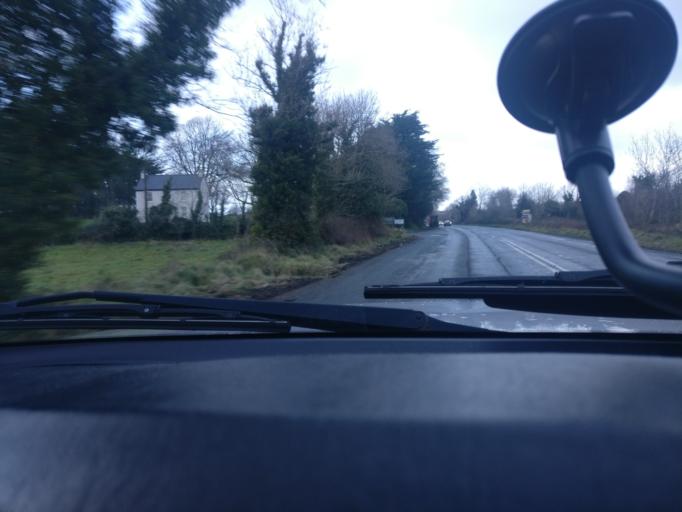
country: IE
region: Connaught
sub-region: County Galway
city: Athenry
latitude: 53.2215
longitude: -8.7175
